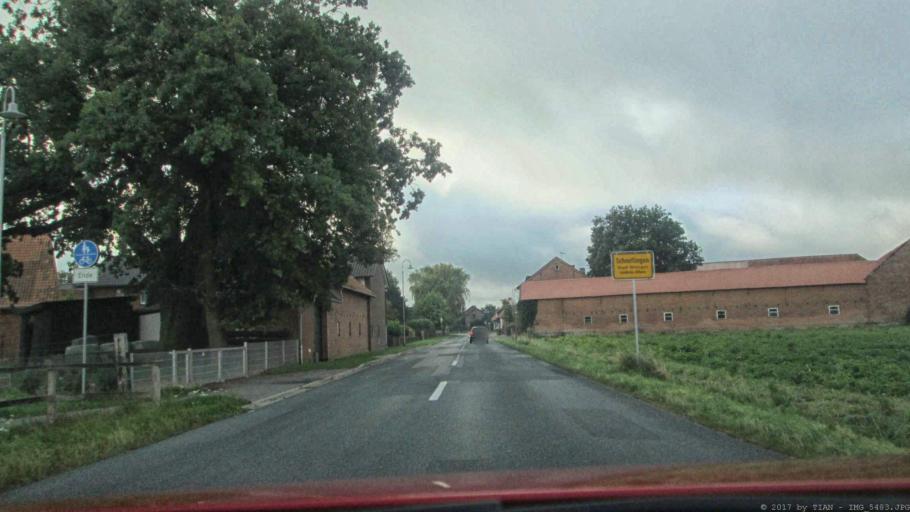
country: DE
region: Lower Saxony
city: Wittingen
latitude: 52.6562
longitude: 10.8024
